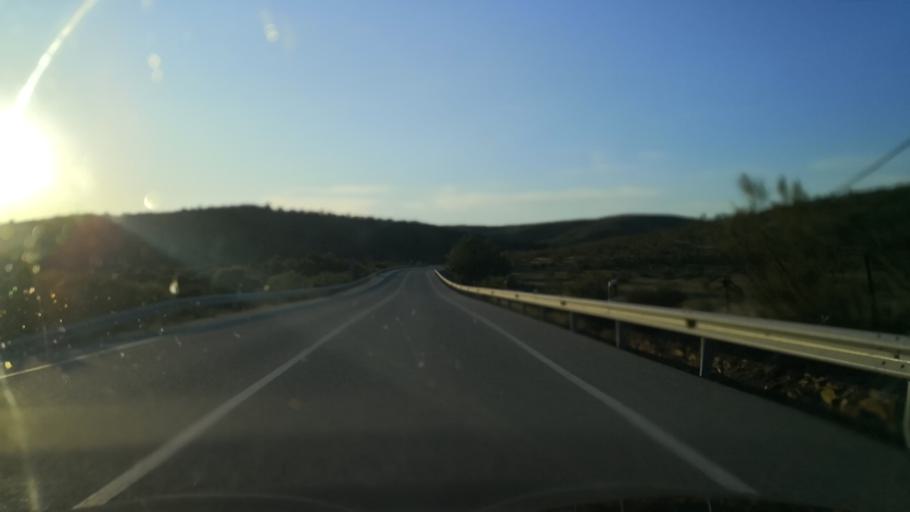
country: ES
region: Extremadura
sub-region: Provincia de Caceres
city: Valencia de Alcantara
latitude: 39.4705
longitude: -7.2087
